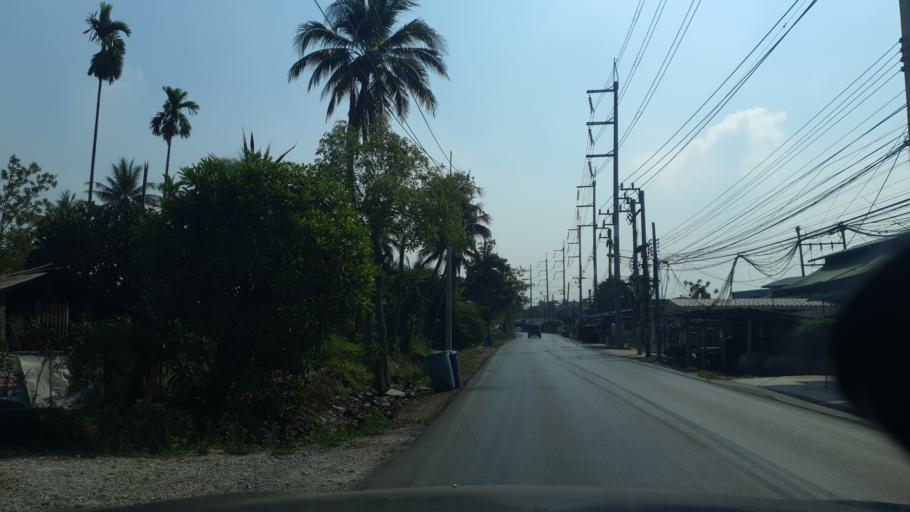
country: TH
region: Nakhon Pathom
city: Salaya
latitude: 13.7755
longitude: 100.2774
